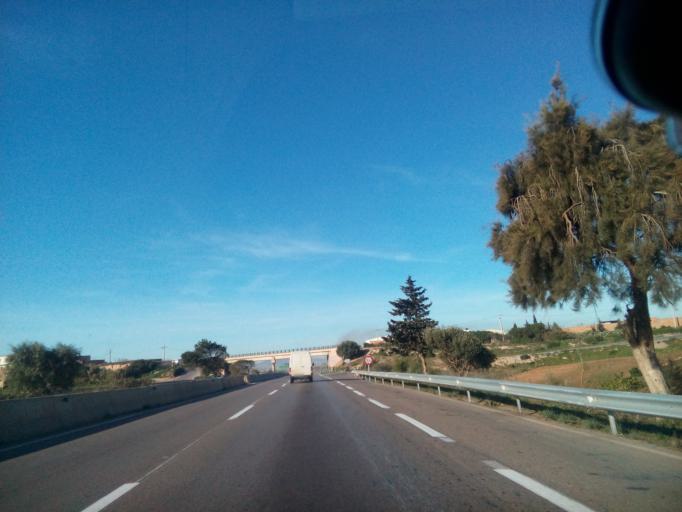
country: DZ
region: Oran
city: Ain el Bya
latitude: 35.7672
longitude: -0.2187
